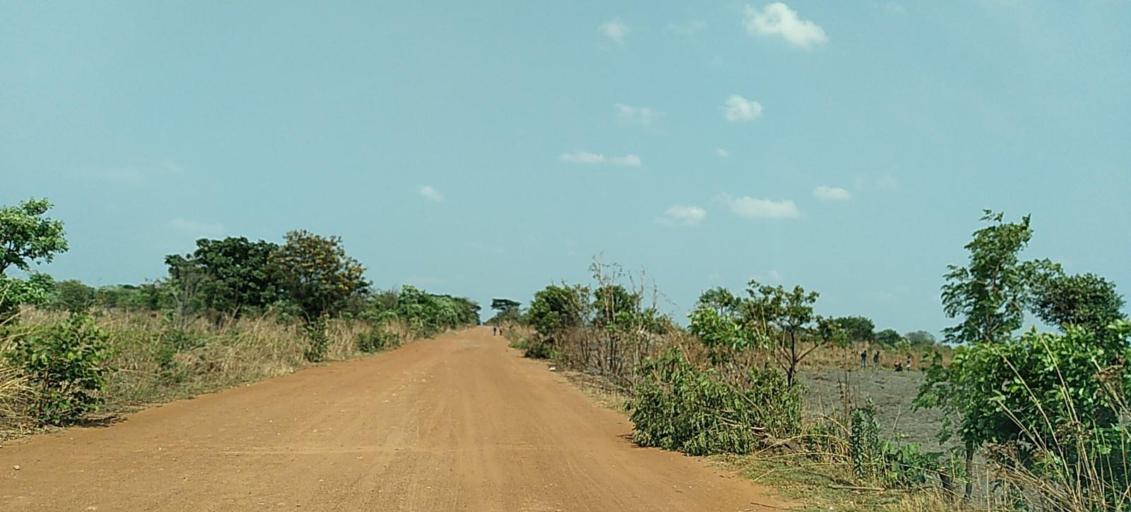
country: ZM
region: Copperbelt
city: Luanshya
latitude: -13.0916
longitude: 28.2946
